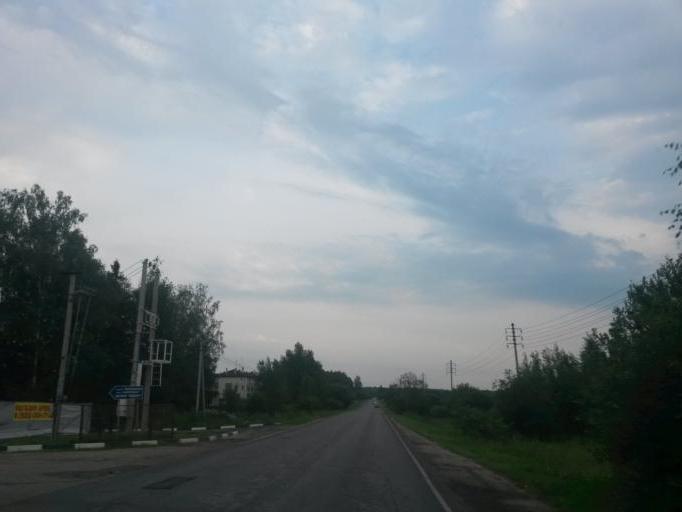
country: RU
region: Moskovskaya
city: L'vovskiy
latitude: 55.3260
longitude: 37.6124
